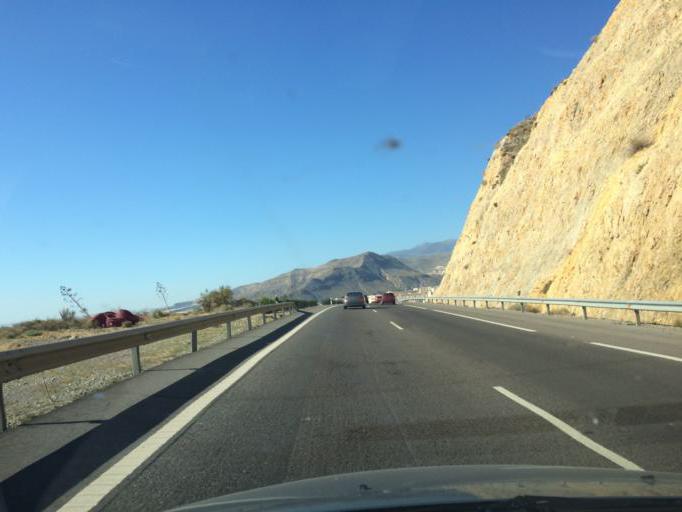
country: ES
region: Andalusia
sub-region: Provincia de Almeria
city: Aguadulce
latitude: 36.8218
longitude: -2.5696
